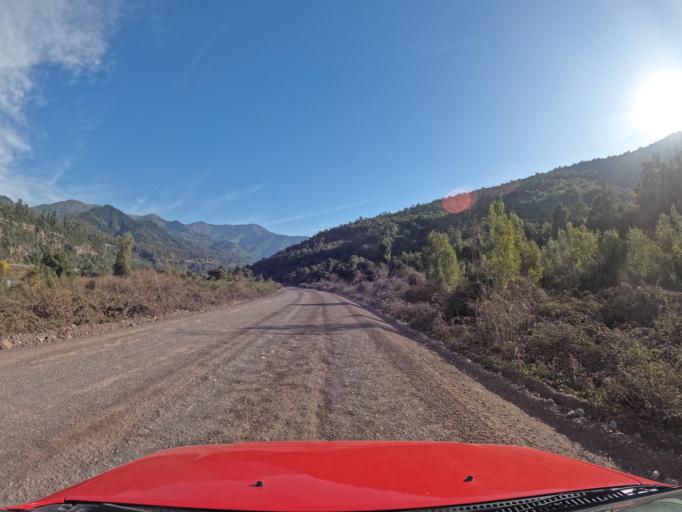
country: CL
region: O'Higgins
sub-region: Provincia de Colchagua
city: Chimbarongo
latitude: -34.9979
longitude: -70.8250
